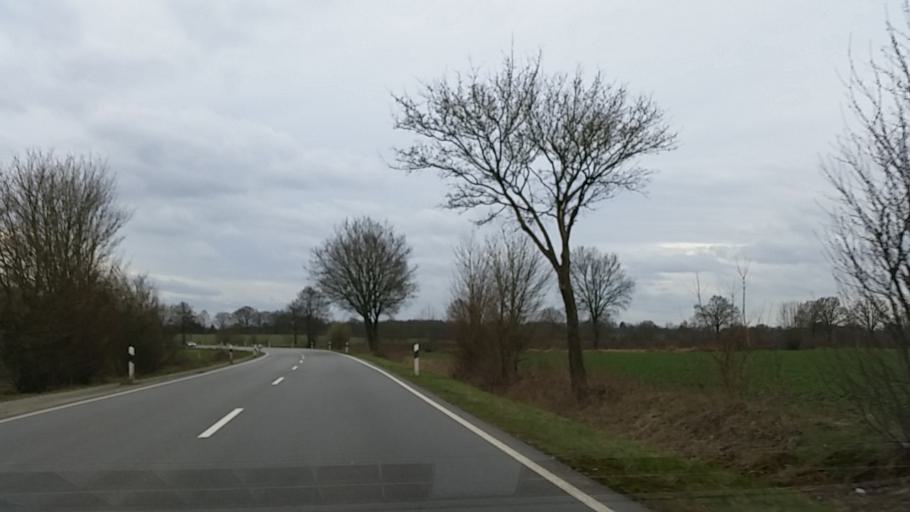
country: DE
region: Schleswig-Holstein
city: Braak
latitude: 53.6050
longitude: 10.2412
